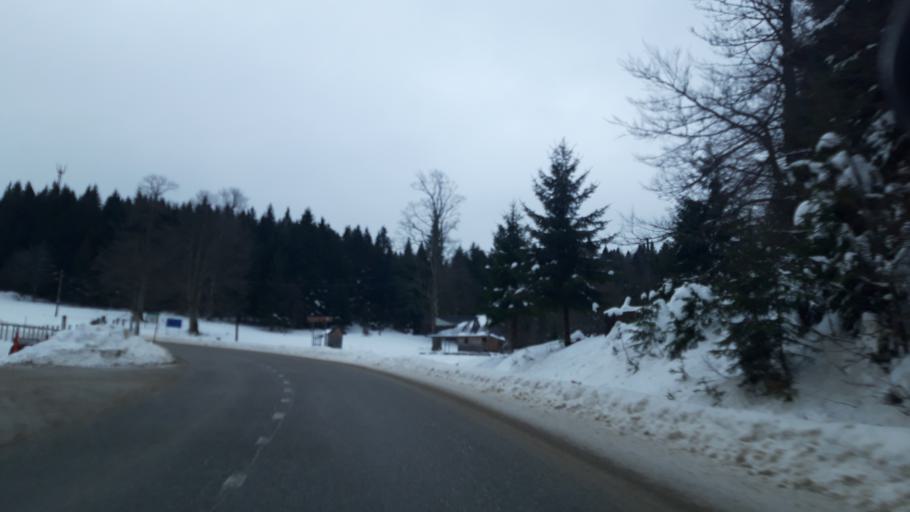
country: BA
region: Republika Srpska
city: Vlasenica
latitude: 44.1456
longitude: 18.9393
